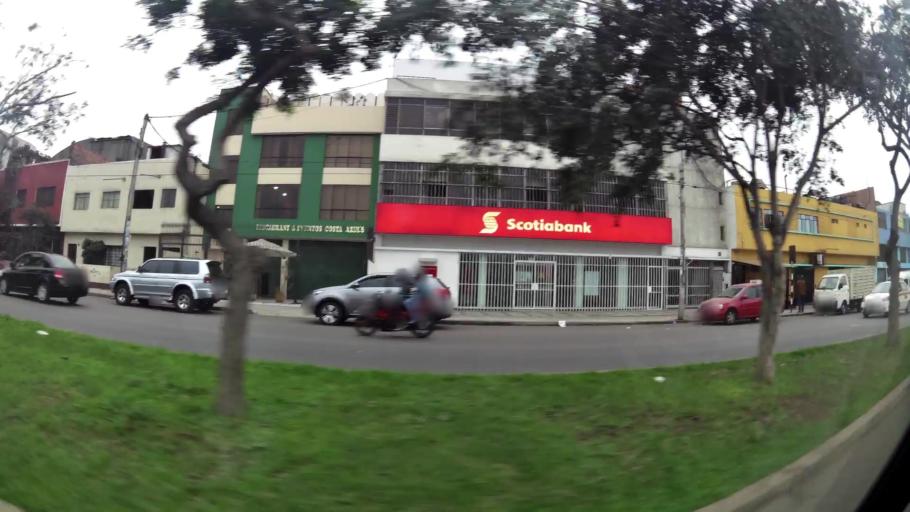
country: PE
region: Lima
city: Lima
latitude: -12.0519
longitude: -77.0607
